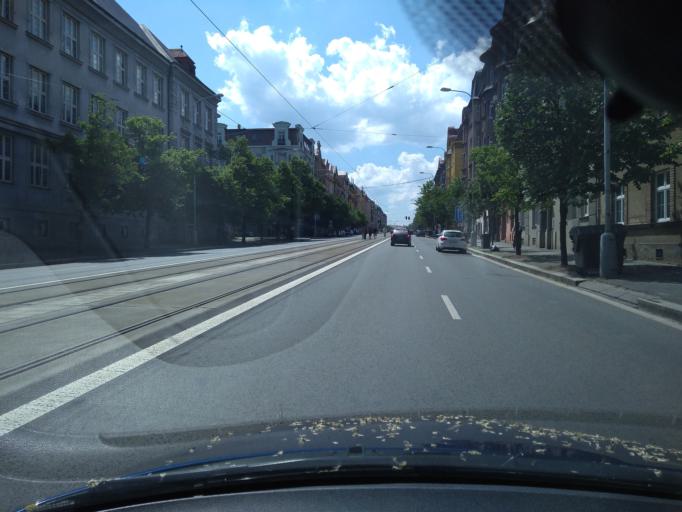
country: CZ
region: Plzensky
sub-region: Okres Plzen-Mesto
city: Pilsen
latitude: 49.7370
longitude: 13.3705
